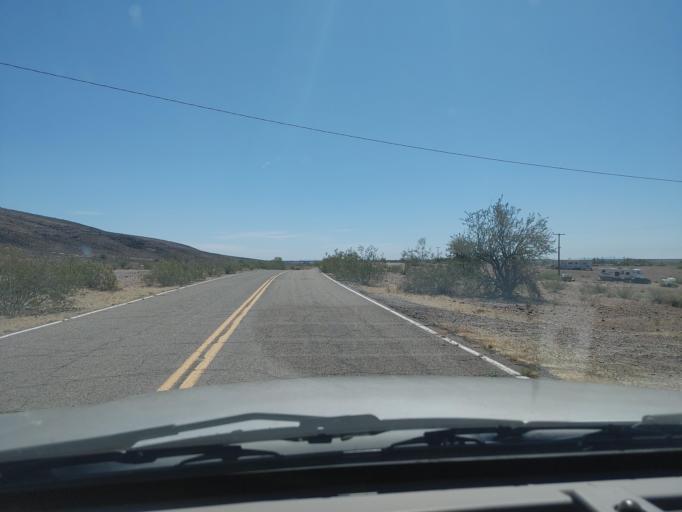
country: US
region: Arizona
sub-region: Maricopa County
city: Gila Bend
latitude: 32.9930
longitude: -113.3381
